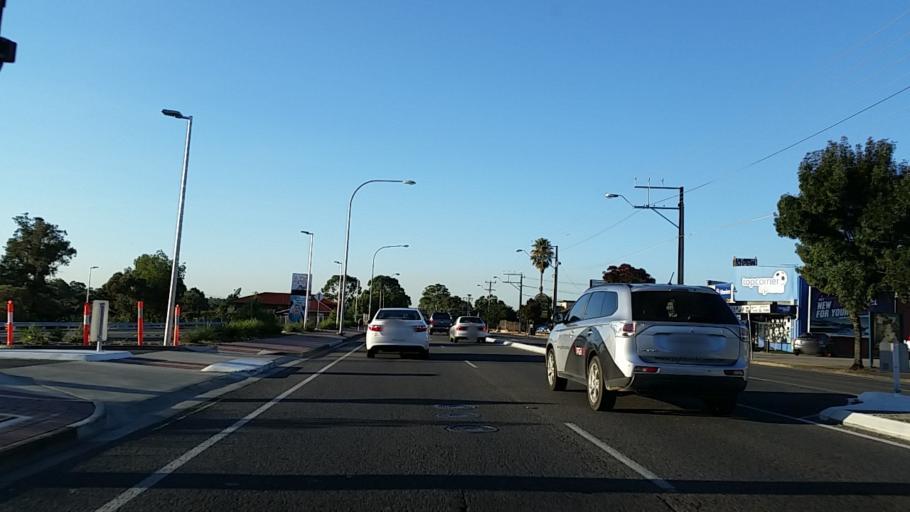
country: AU
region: South Australia
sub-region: Campbelltown
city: Hectorville
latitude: -34.8858
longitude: 138.6588
